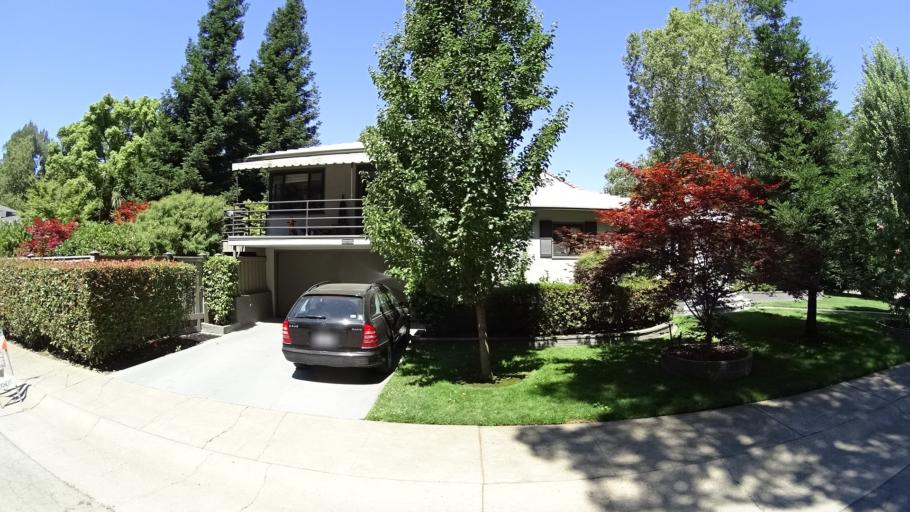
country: US
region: California
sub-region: Sacramento County
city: Sacramento
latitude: 38.5464
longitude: -121.5005
